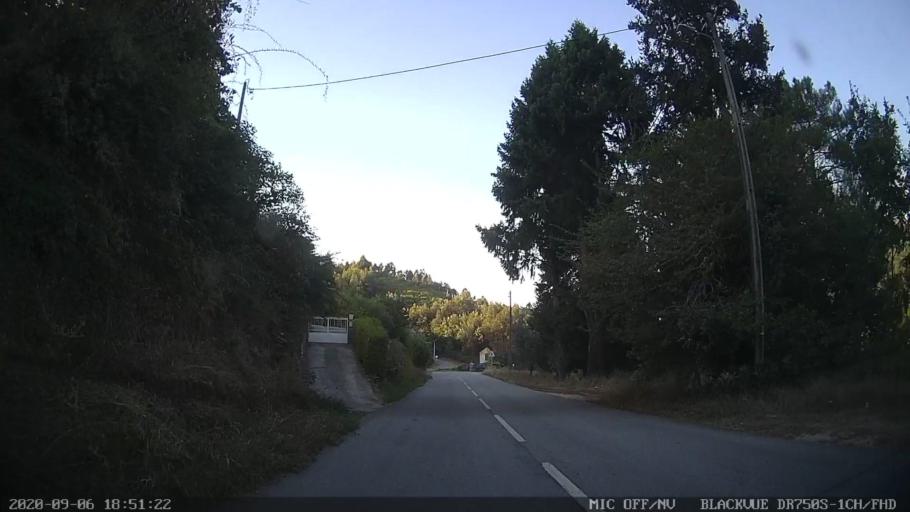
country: PT
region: Porto
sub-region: Amarante
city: Amarante
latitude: 41.2582
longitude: -7.9918
